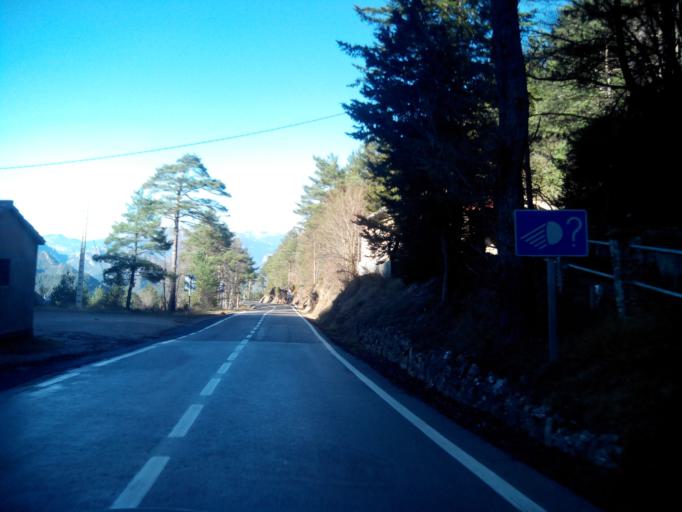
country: ES
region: Catalonia
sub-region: Provincia de Barcelona
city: Capolat
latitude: 42.0936
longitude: 1.7606
